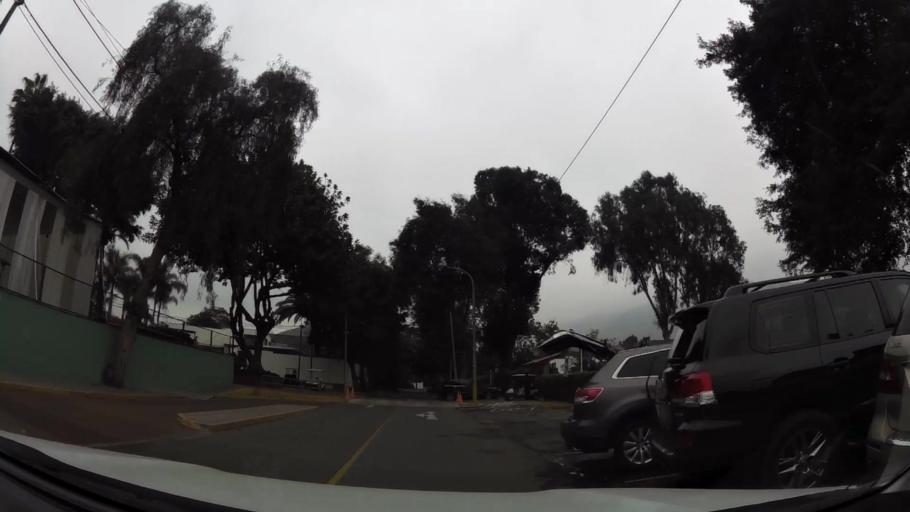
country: PE
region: Lima
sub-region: Lima
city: La Molina
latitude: -12.0752
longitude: -76.9082
